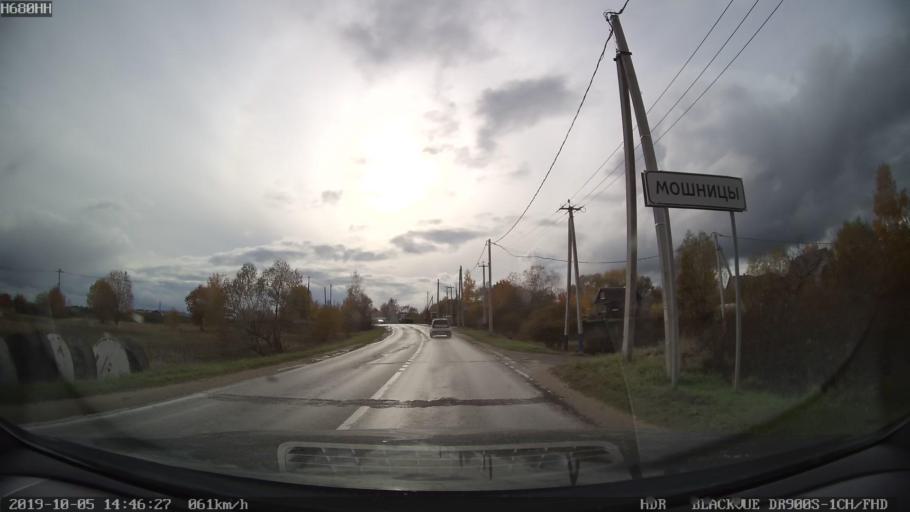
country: RU
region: Moskovskaya
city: Solnechnogorsk
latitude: 56.2263
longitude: 36.9083
